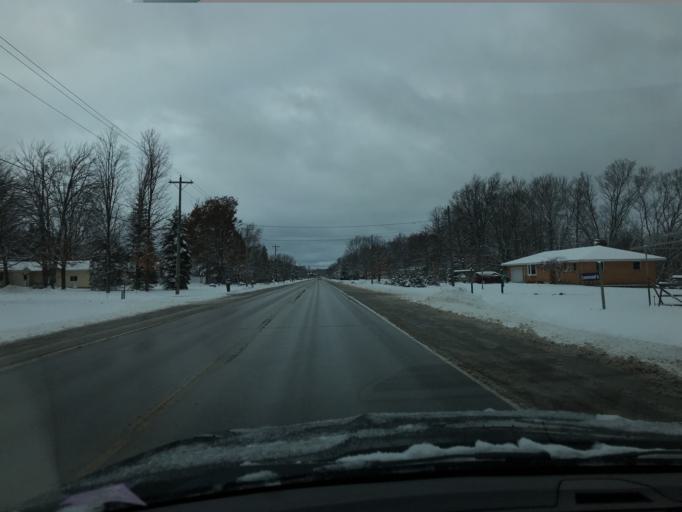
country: US
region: Michigan
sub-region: Charlevoix County
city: Charlevoix
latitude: 45.2886
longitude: -85.2456
